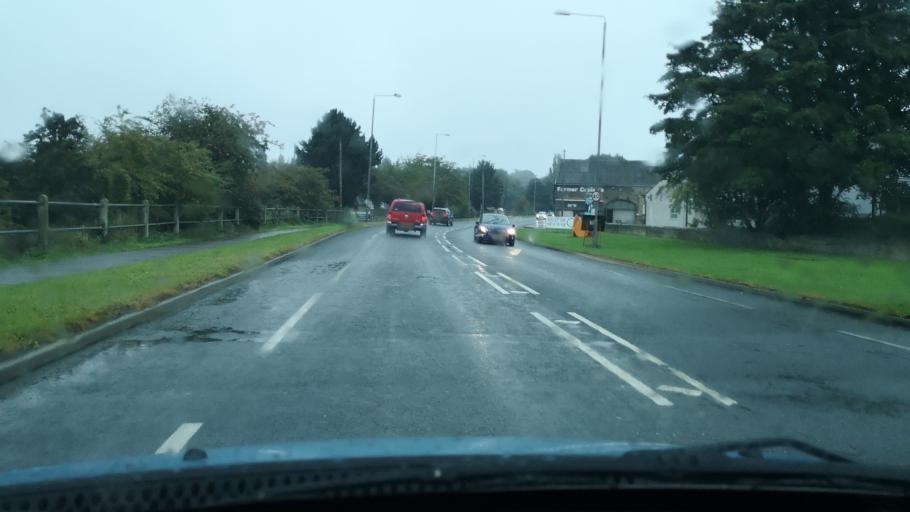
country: GB
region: England
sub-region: City and Borough of Wakefield
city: Featherstone
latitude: 53.6797
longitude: -1.3368
